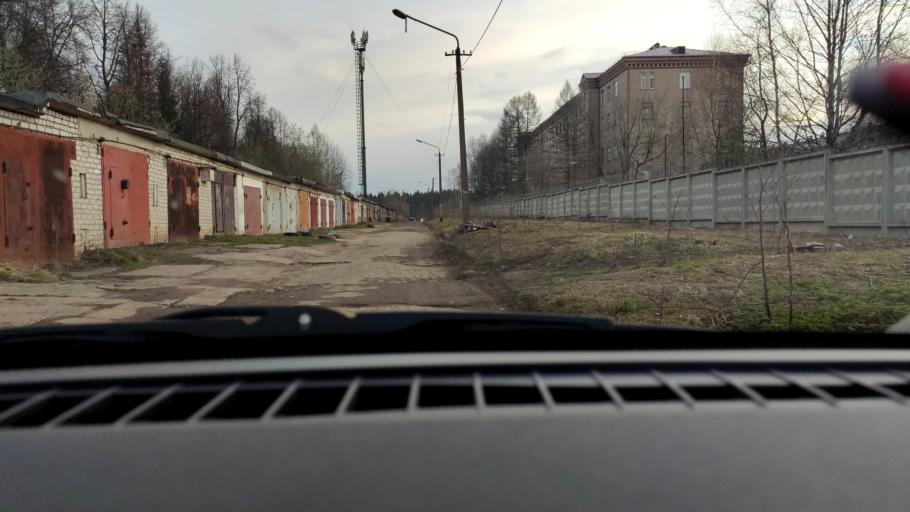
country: RU
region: Perm
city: Froly
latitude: 57.9720
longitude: 56.3210
